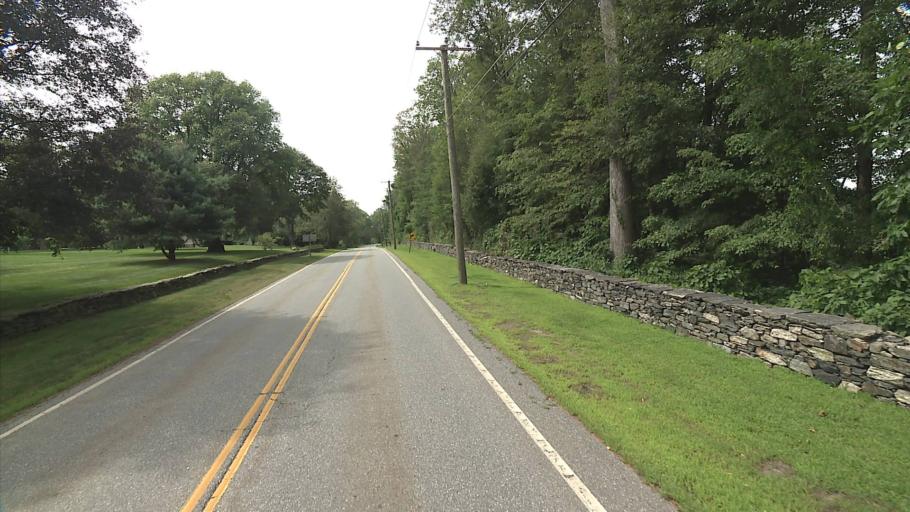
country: US
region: Connecticut
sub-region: Windham County
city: Thompson
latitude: 41.9533
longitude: -71.8668
